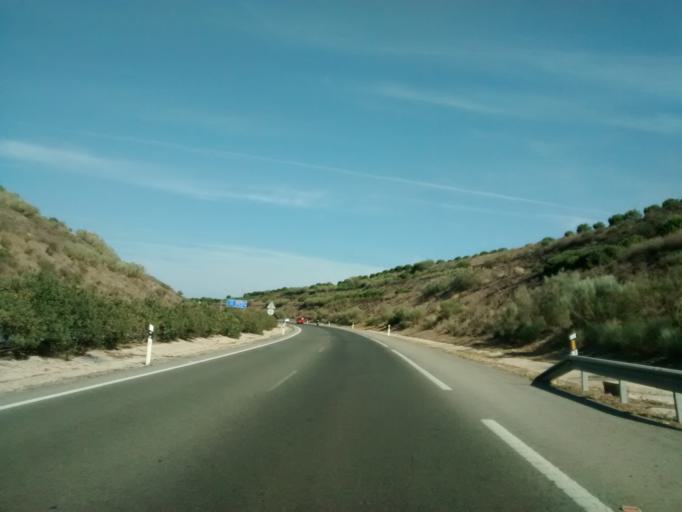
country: ES
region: Andalusia
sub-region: Provincia de Cadiz
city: Conil de la Frontera
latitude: 36.3407
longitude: -6.0496
